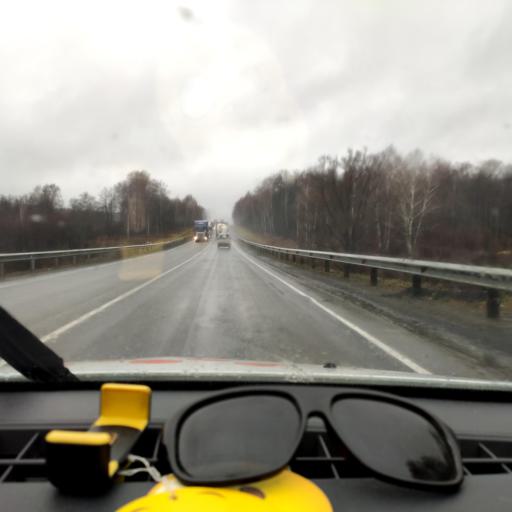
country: RU
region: Bashkortostan
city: Iglino
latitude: 54.7841
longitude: 56.5262
